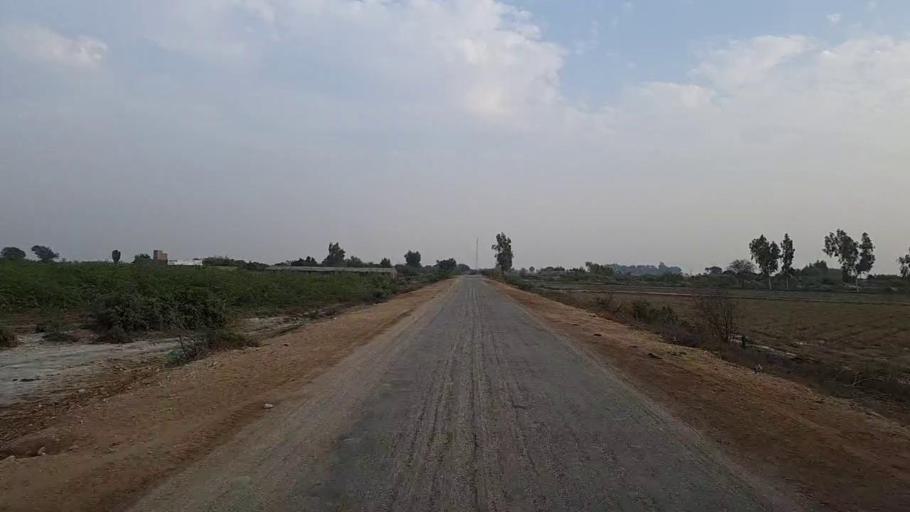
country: PK
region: Sindh
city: Samaro
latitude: 25.3875
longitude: 69.3263
